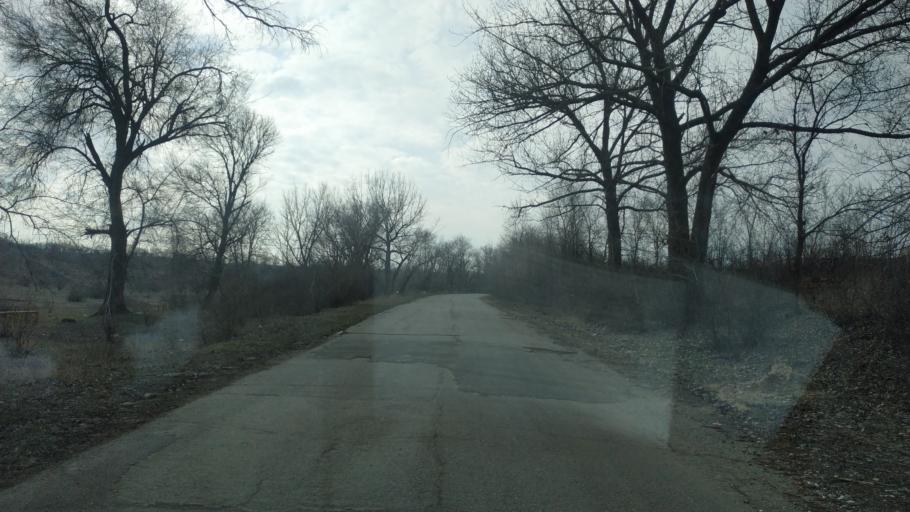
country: MD
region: Chisinau
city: Vadul lui Voda
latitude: 46.9996
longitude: 29.1113
